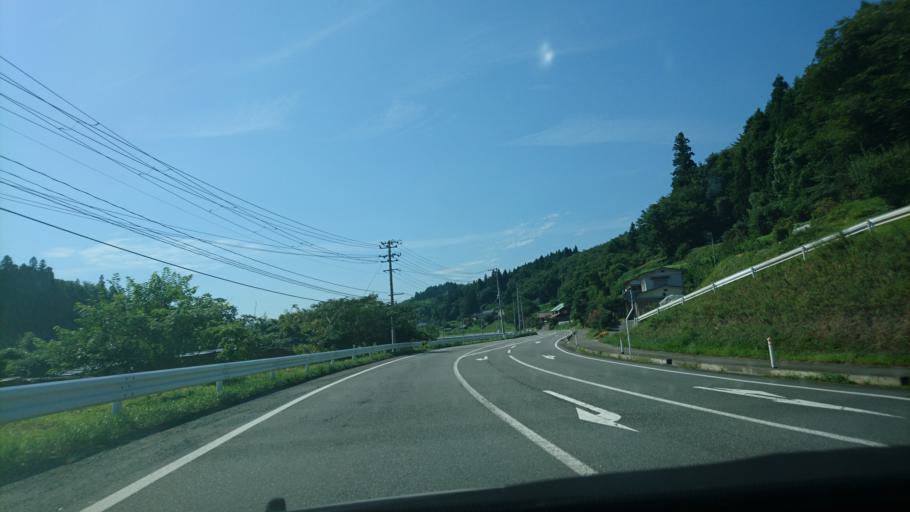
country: JP
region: Iwate
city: Ichinoseki
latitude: 38.9988
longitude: 141.3521
